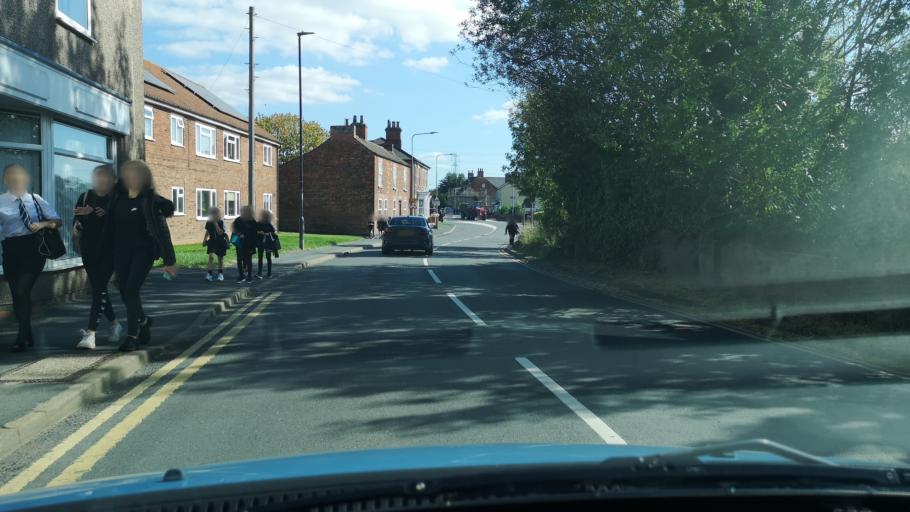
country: GB
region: England
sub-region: North Lincolnshire
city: Crowle
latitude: 53.6049
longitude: -0.8326
